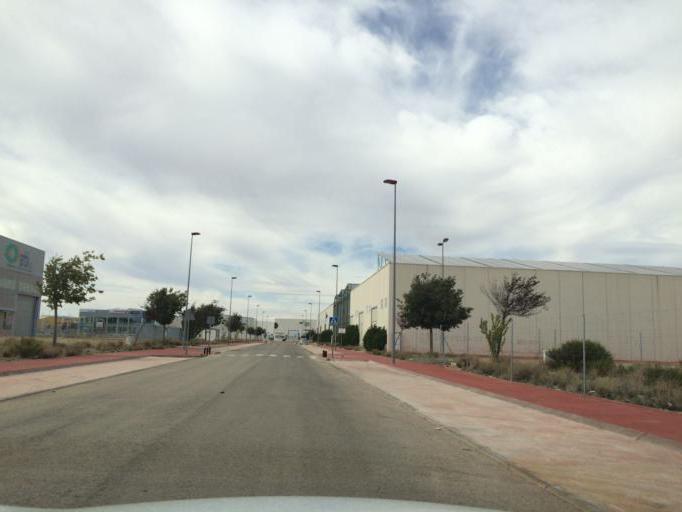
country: ES
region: Castille-La Mancha
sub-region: Provincia de Albacete
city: Albacete
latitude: 39.0269
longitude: -1.8877
